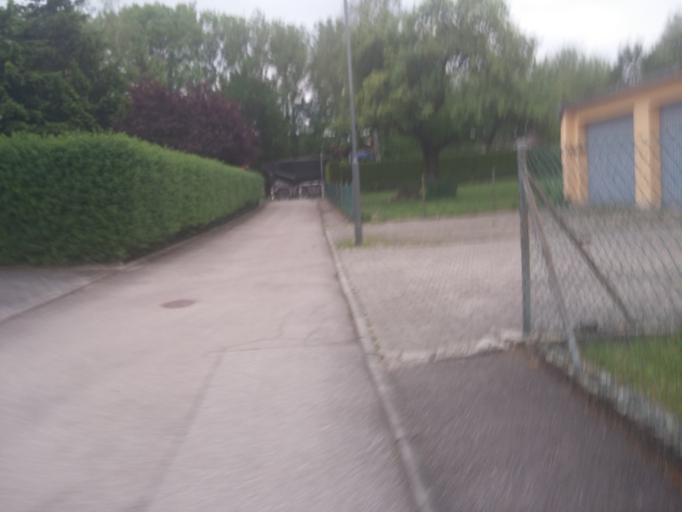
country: DE
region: Bavaria
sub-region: Upper Bavaria
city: Dachau
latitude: 48.2573
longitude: 11.4578
